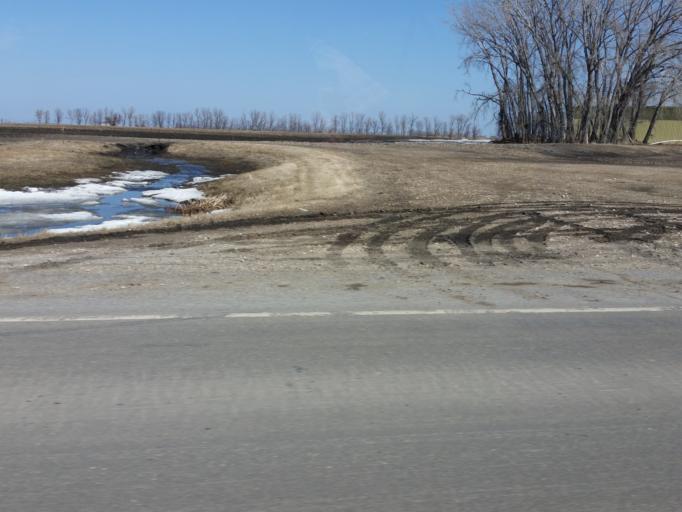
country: US
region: North Dakota
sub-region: Walsh County
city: Grafton
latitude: 48.2970
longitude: -97.3741
